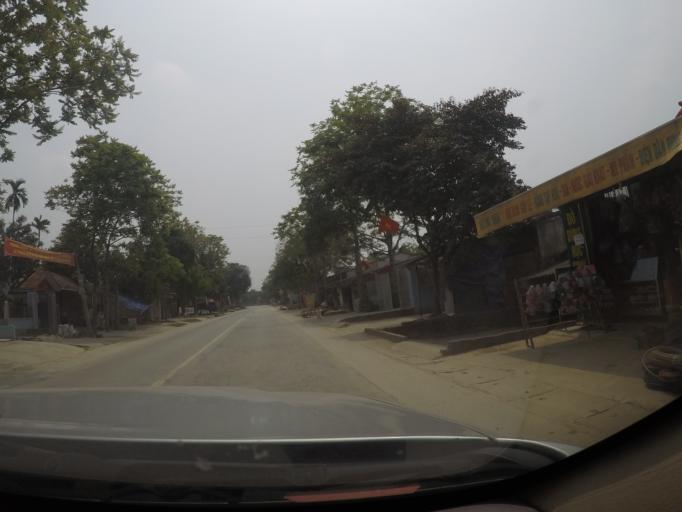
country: VN
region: Thanh Hoa
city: Thi Tran Thuong Xuan
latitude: 19.8023
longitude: 105.3962
